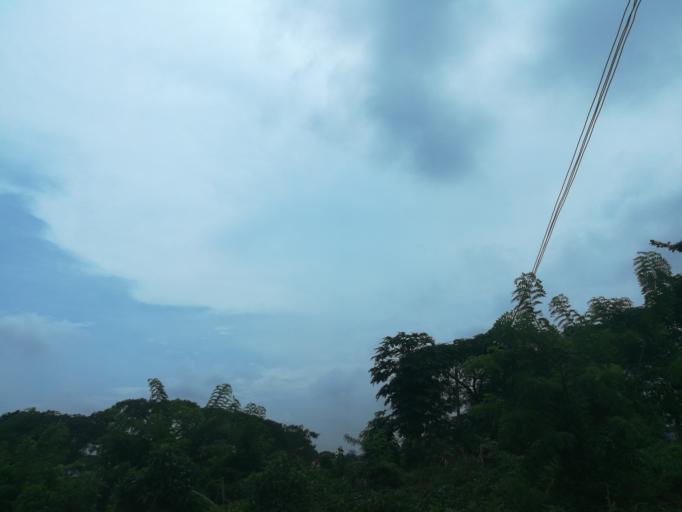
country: NG
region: Lagos
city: Oshodi
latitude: 6.5667
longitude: 3.3576
